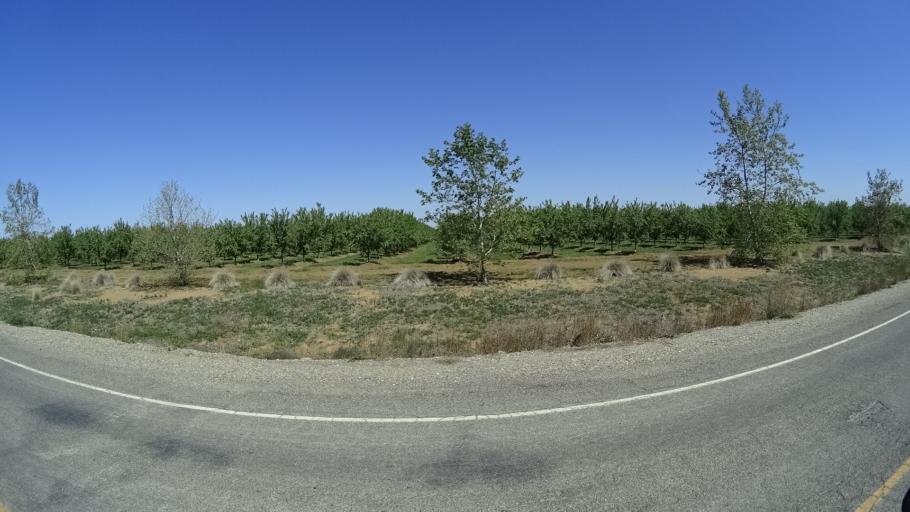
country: US
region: California
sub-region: Glenn County
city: Willows
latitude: 39.5388
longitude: -122.2117
